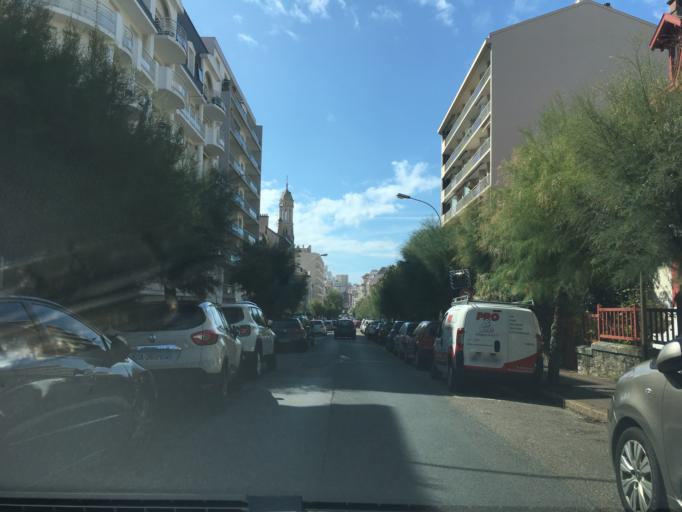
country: FR
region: Aquitaine
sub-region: Departement des Pyrenees-Atlantiques
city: Biarritz
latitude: 43.4853
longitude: -1.5499
